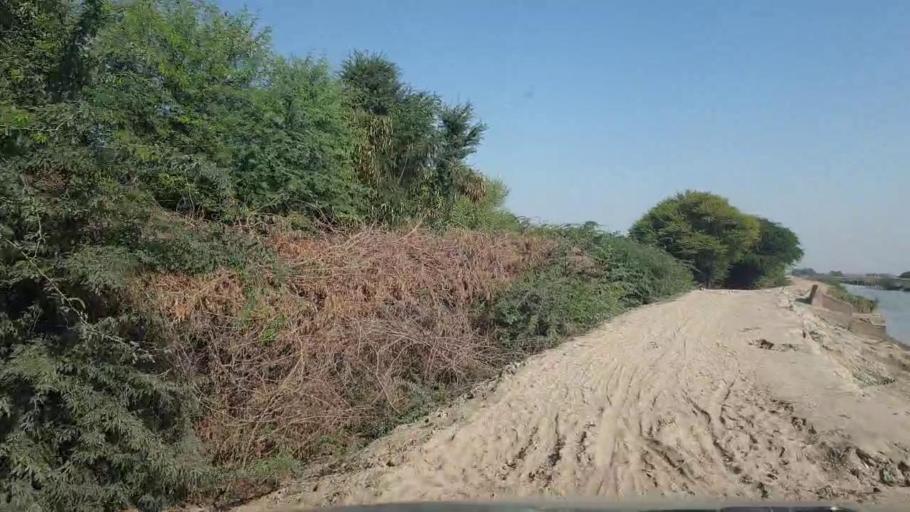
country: PK
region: Sindh
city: Badin
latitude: 24.7238
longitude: 68.8029
